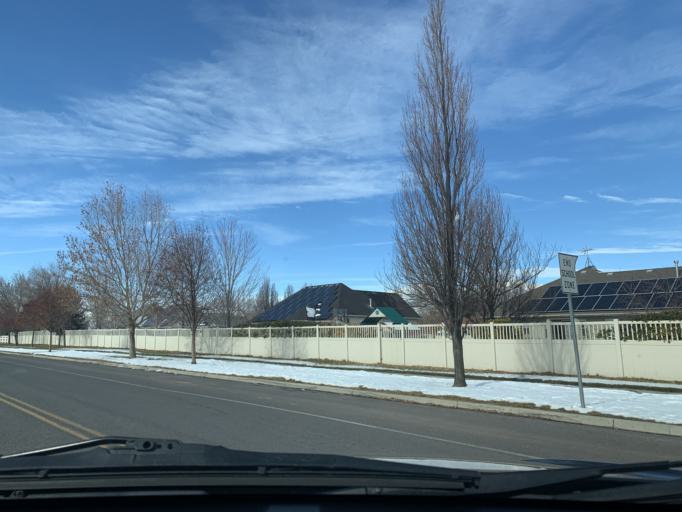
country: US
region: Utah
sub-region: Utah County
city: Lehi
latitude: 40.4209
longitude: -111.8212
